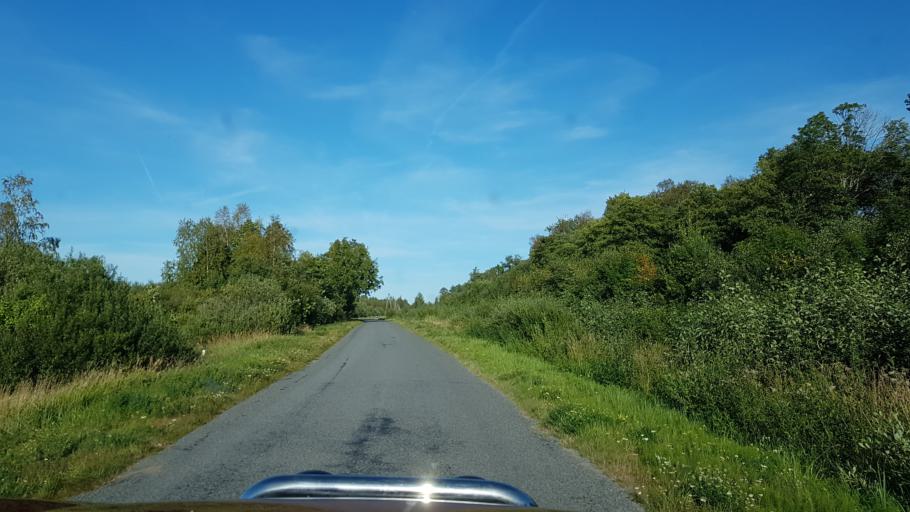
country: LV
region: Salacgrivas
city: Ainazi
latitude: 57.8763
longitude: 24.3731
